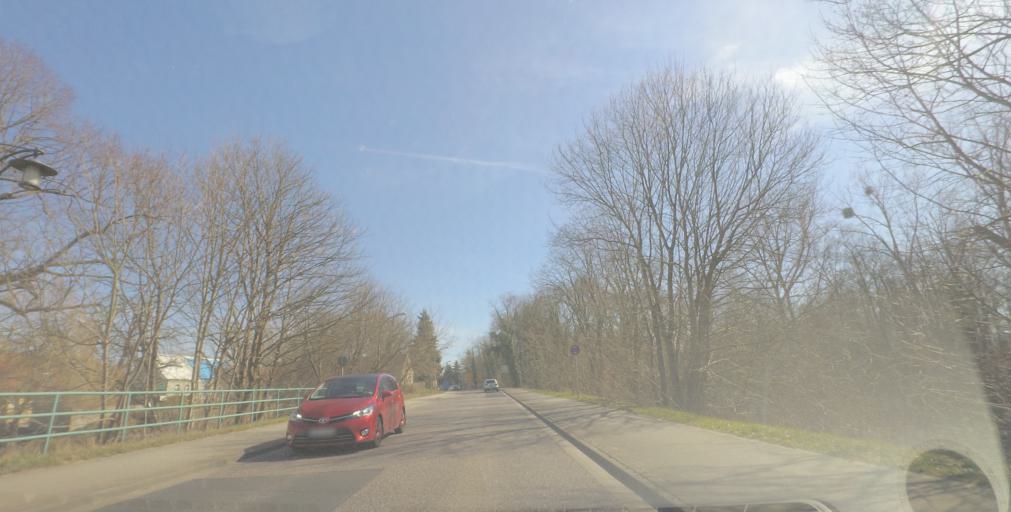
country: DE
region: Brandenburg
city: Neuruppin
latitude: 52.9468
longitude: 12.8460
